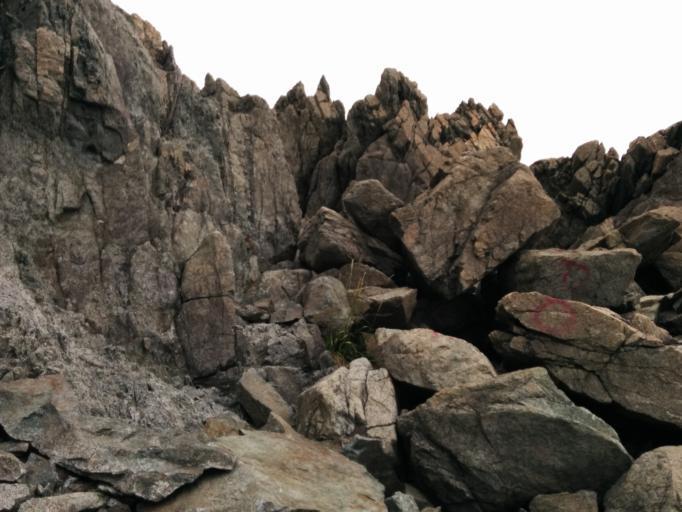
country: JP
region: Hokkaido
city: Iwanai
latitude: 42.3063
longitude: 139.7670
